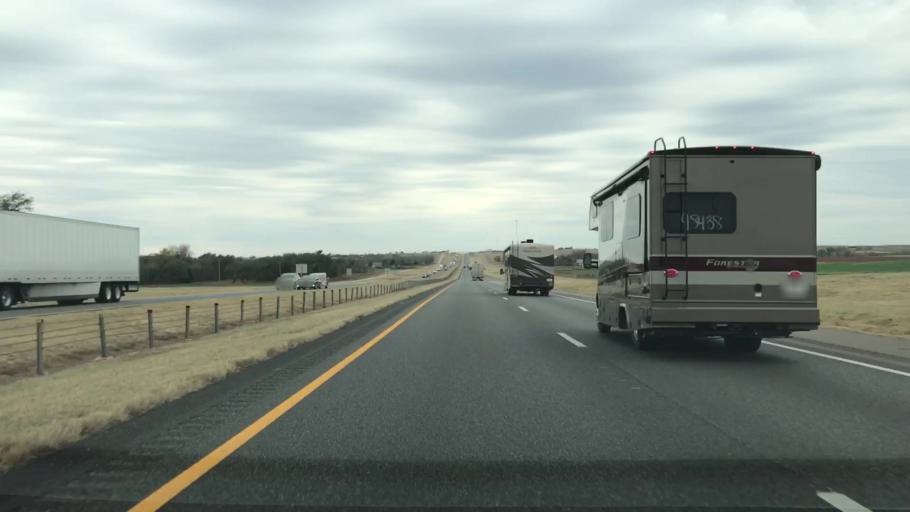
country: US
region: Oklahoma
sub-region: Custer County
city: Clinton
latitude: 35.5160
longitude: -98.8722
